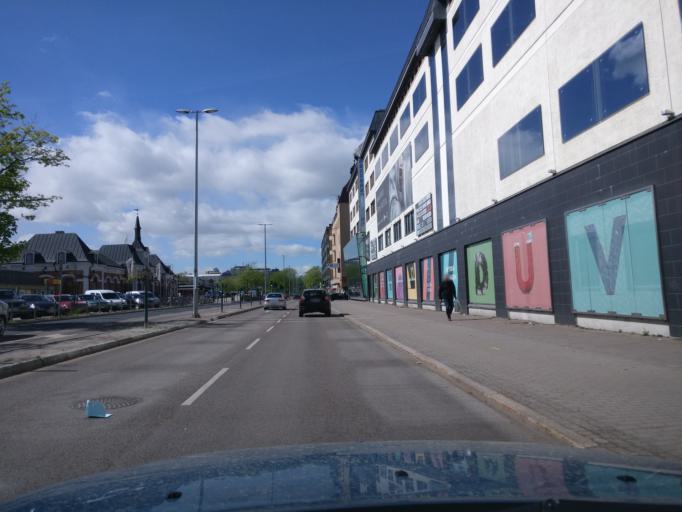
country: SE
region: Vaermland
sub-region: Karlstads Kommun
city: Karlstad
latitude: 59.3783
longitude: 13.5010
